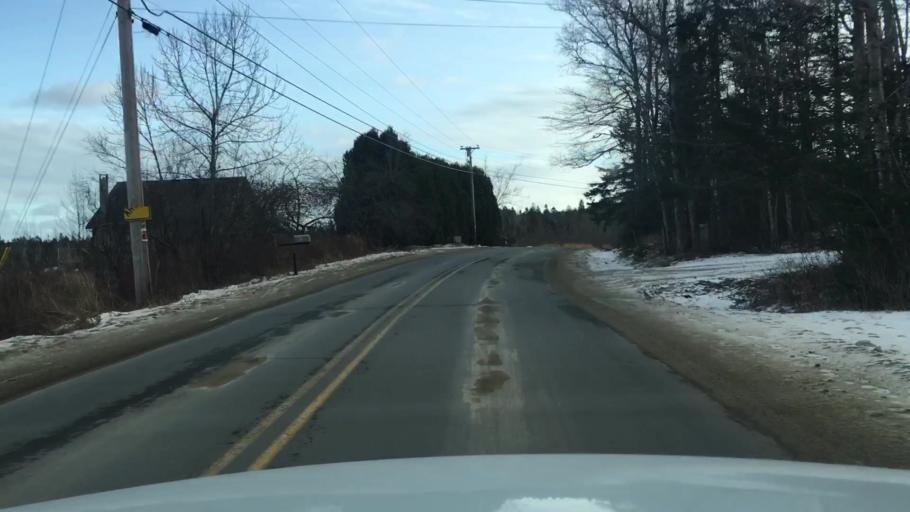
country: US
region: Maine
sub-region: Washington County
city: Jonesport
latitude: 44.6139
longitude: -67.6030
